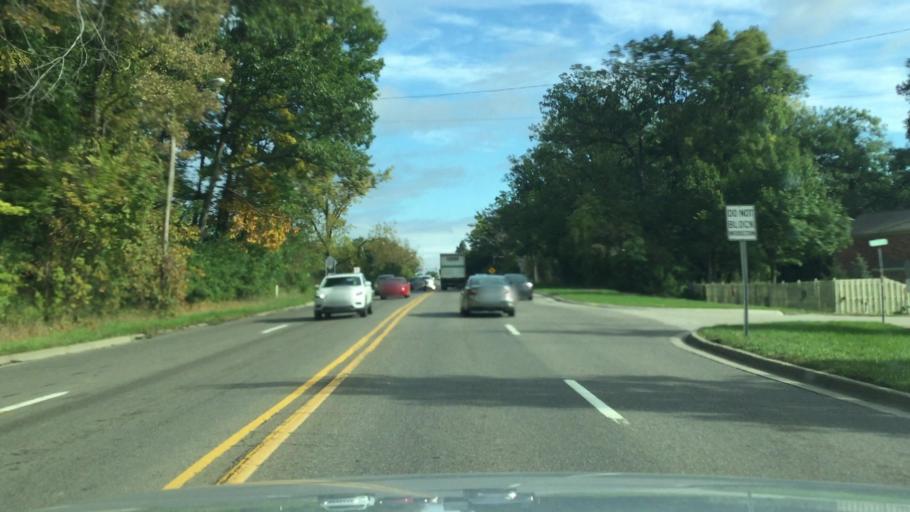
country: US
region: Michigan
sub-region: Oakland County
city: Orchard Lake
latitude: 42.5797
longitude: -83.3619
